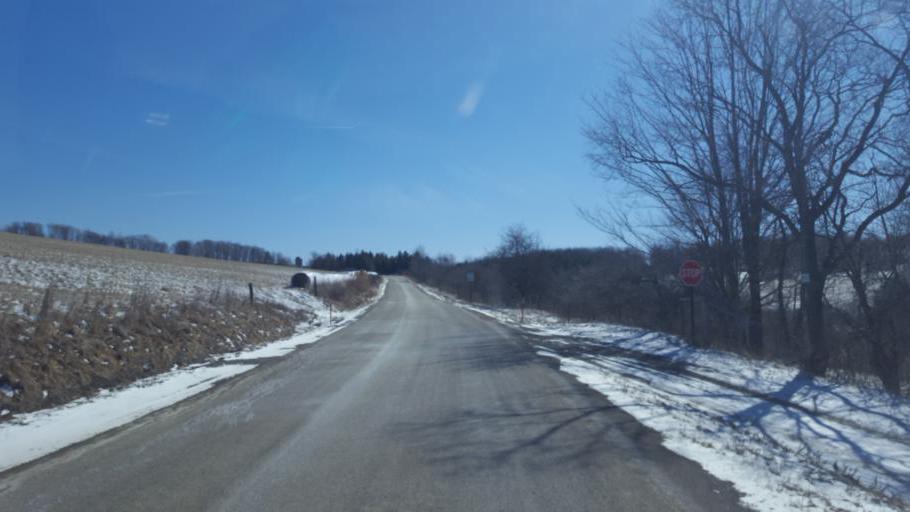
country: US
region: New York
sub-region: Allegany County
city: Andover
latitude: 41.9967
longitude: -77.7690
